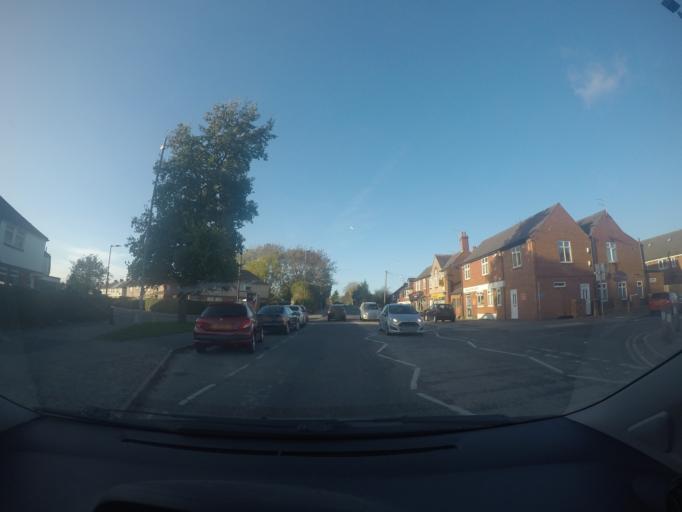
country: GB
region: England
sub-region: City of York
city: Heslington
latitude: 53.9590
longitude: -1.0499
